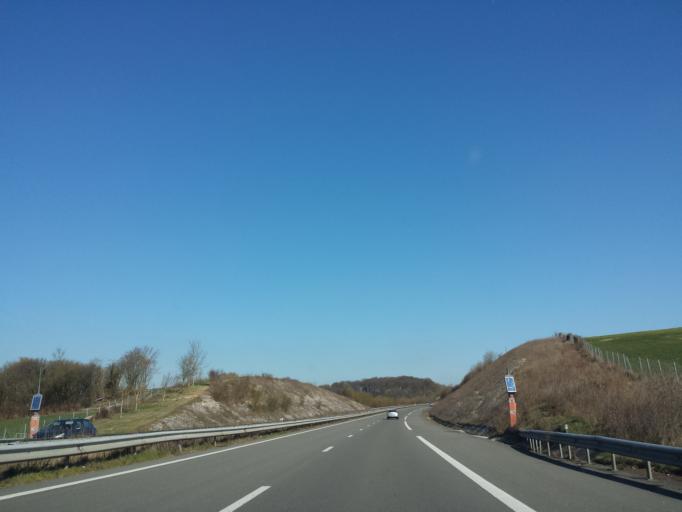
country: FR
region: Picardie
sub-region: Departement de la Somme
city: Conty
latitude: 49.6740
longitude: 2.2102
